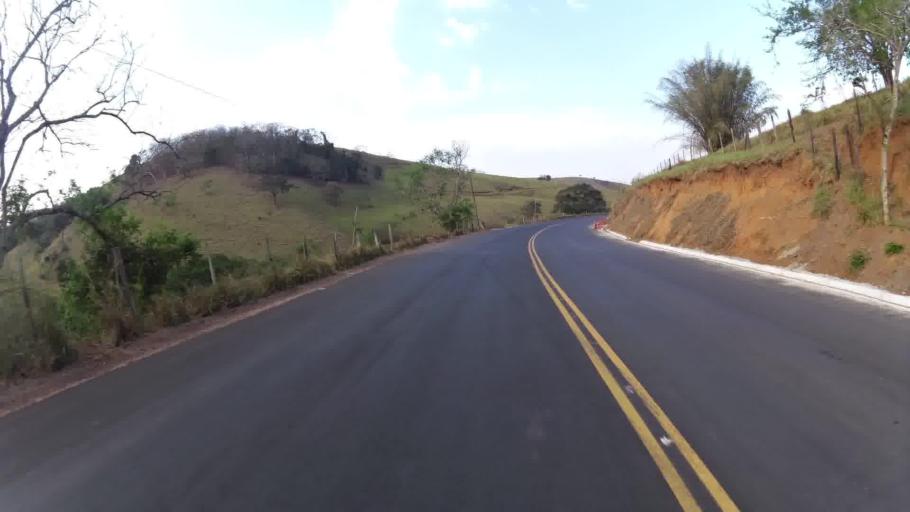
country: BR
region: Rio de Janeiro
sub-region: Santo Antonio De Padua
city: Santo Antonio de Padua
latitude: -21.4904
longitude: -42.0710
